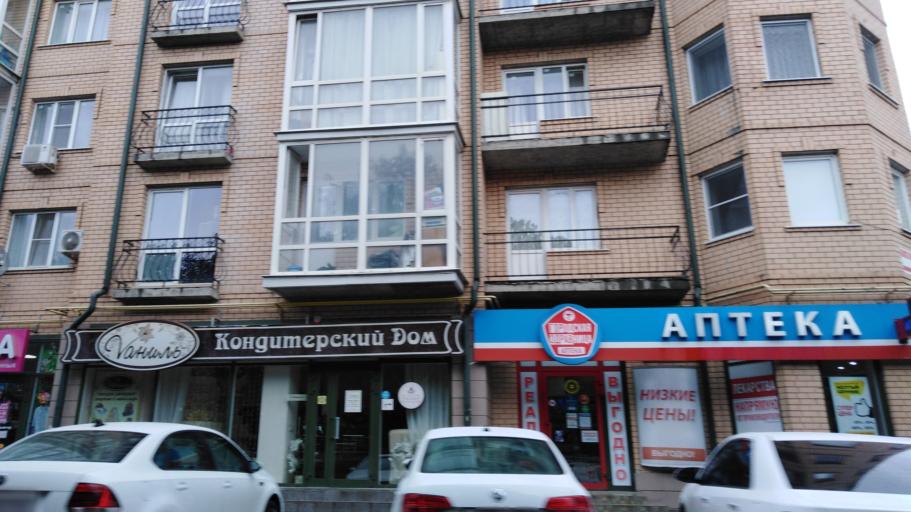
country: RU
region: Stavropol'skiy
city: Yessentukskaya
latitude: 44.0490
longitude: 42.8954
